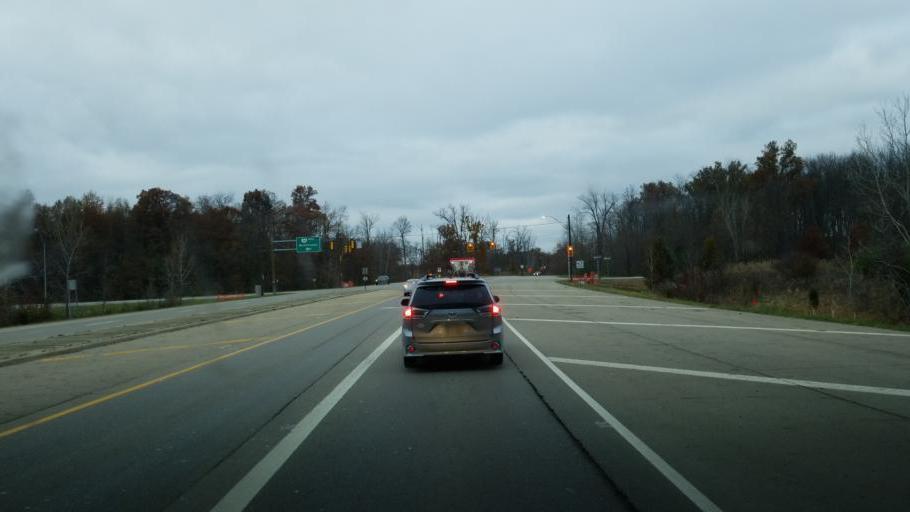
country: US
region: Ohio
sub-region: Franklin County
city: New Albany
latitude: 40.0840
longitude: -82.8537
